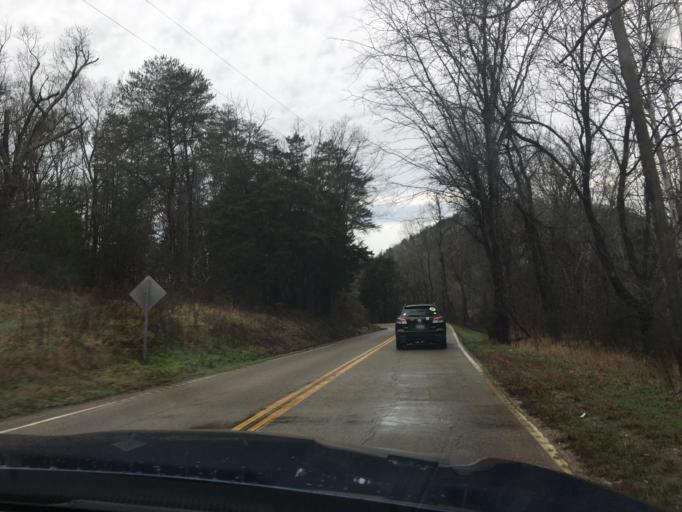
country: US
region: Tennessee
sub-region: McMinn County
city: Englewood
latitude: 35.3564
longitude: -84.4133
